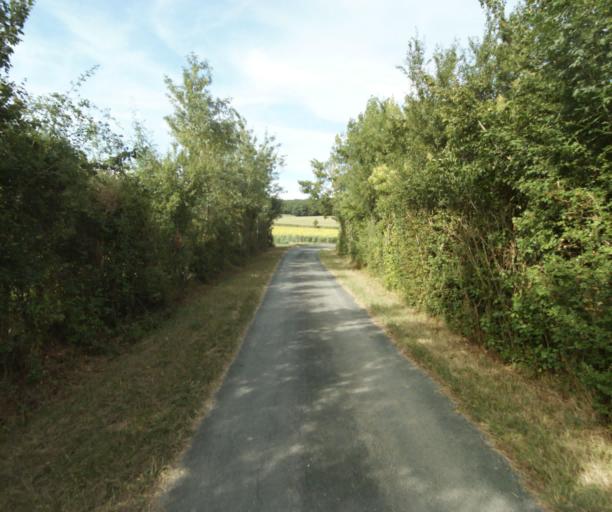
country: FR
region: Midi-Pyrenees
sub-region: Departement du Tarn
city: Puylaurens
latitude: 43.5286
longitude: 2.0444
